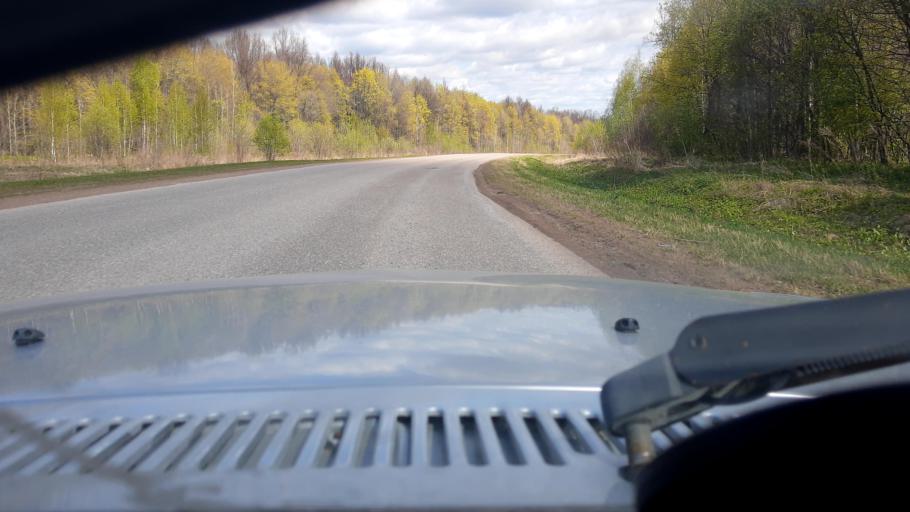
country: RU
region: Bashkortostan
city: Blagoveshchensk
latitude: 55.1107
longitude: 56.0567
